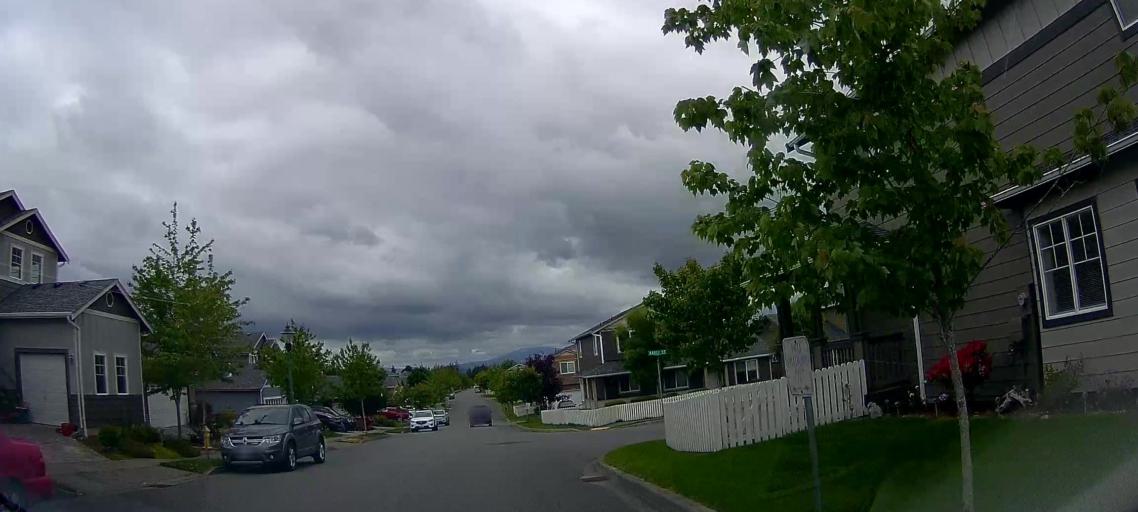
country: US
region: Washington
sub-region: Skagit County
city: Big Lake
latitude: 48.4151
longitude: -122.2831
